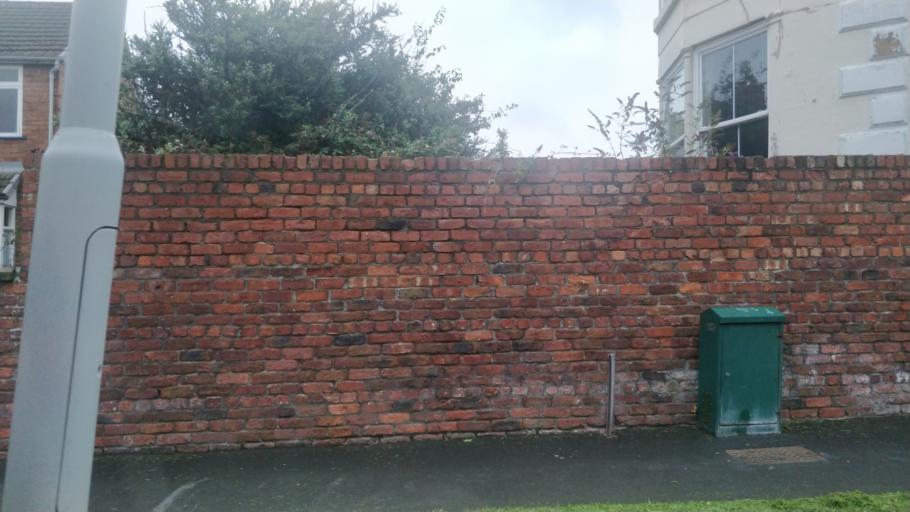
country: GB
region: England
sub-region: Sefton
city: Maghull
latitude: 53.5189
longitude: -2.9467
